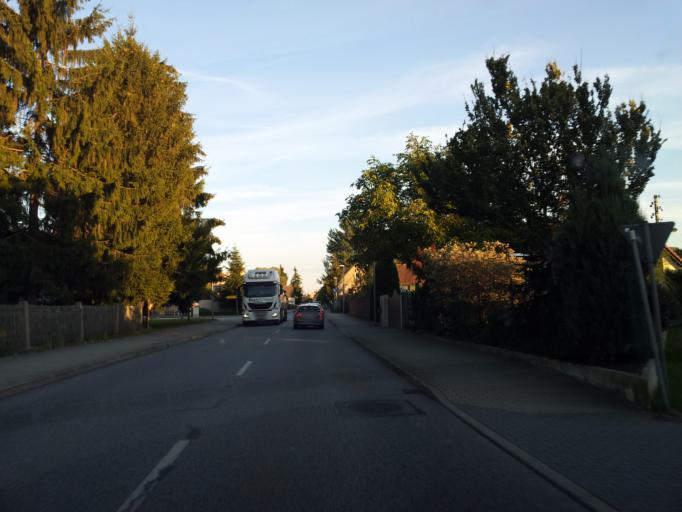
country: DE
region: Saxony
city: Ottendorf-Okrilla
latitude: 51.1850
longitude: 13.8413
